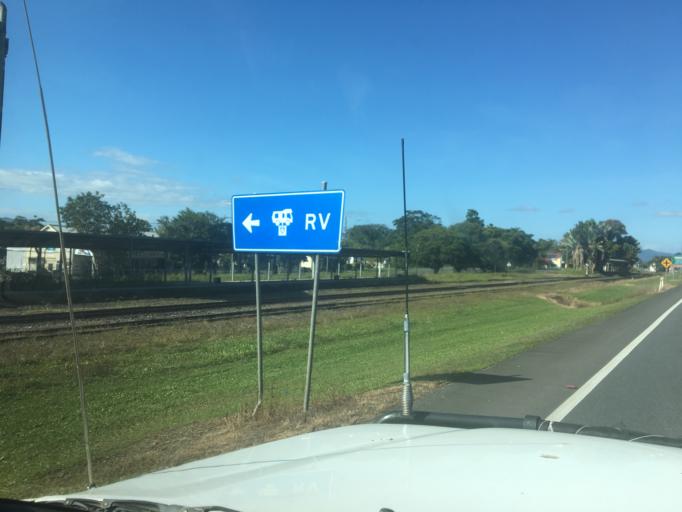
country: AU
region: Queensland
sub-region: Cassowary Coast
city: Innisfail
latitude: -17.3415
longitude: 145.9254
